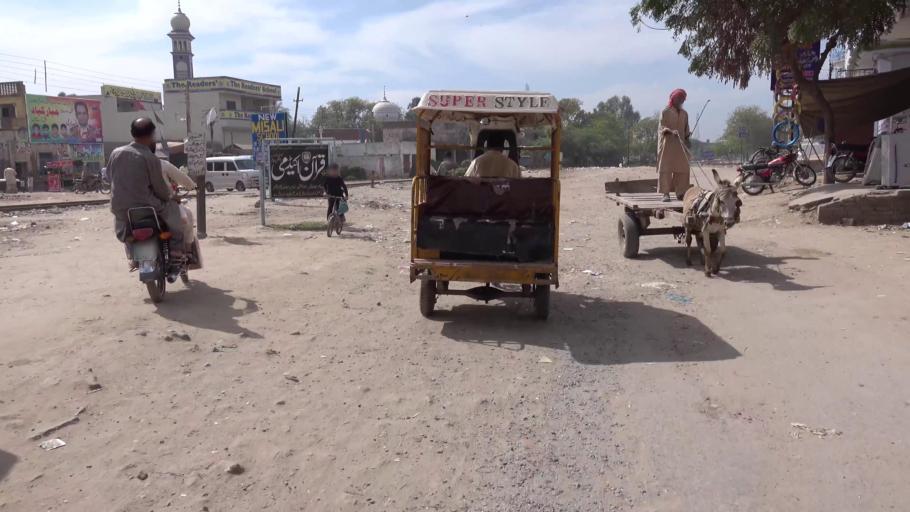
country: PK
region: Punjab
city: Hafizabad
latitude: 32.0670
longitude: 73.6853
